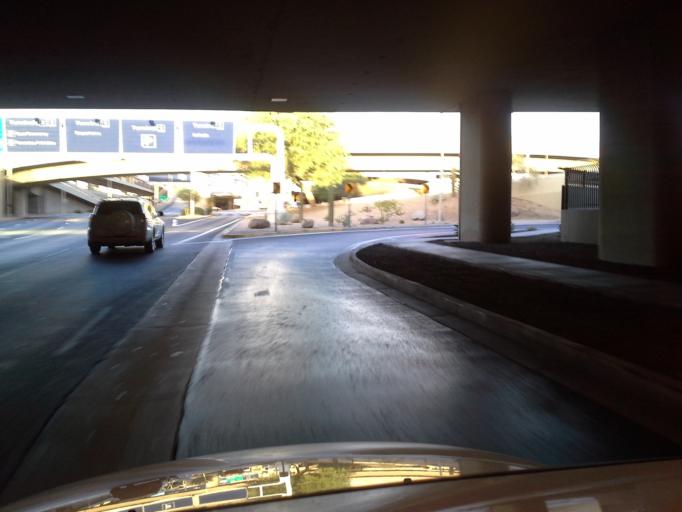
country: US
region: Arizona
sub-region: Maricopa County
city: Tempe Junction
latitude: 33.4358
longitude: -112.0038
